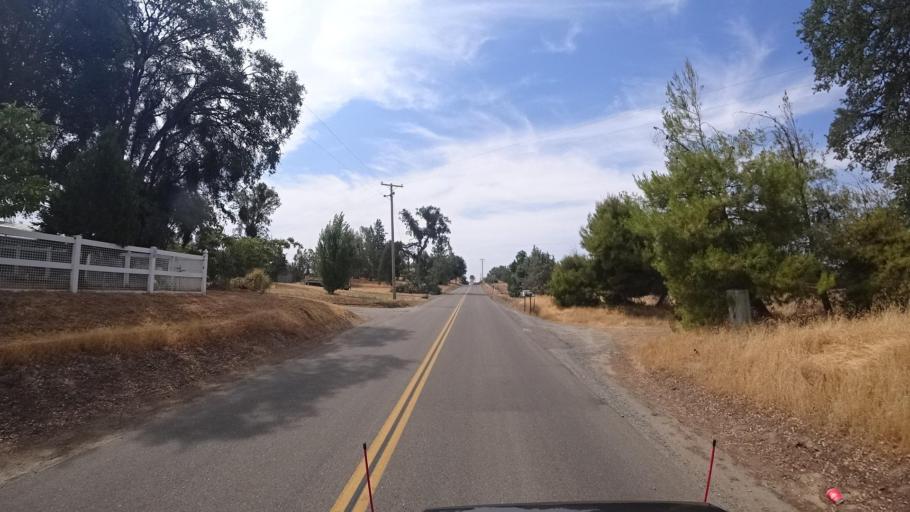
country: US
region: California
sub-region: Mariposa County
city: Midpines
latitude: 37.4717
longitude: -119.8872
